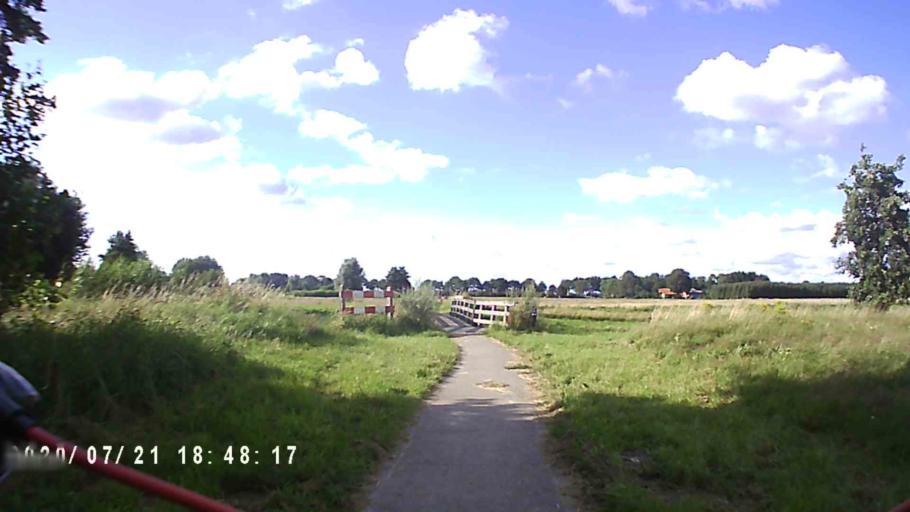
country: NL
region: Groningen
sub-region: Gemeente Hoogezand-Sappemeer
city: Hoogezand
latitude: 53.2158
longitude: 6.7477
